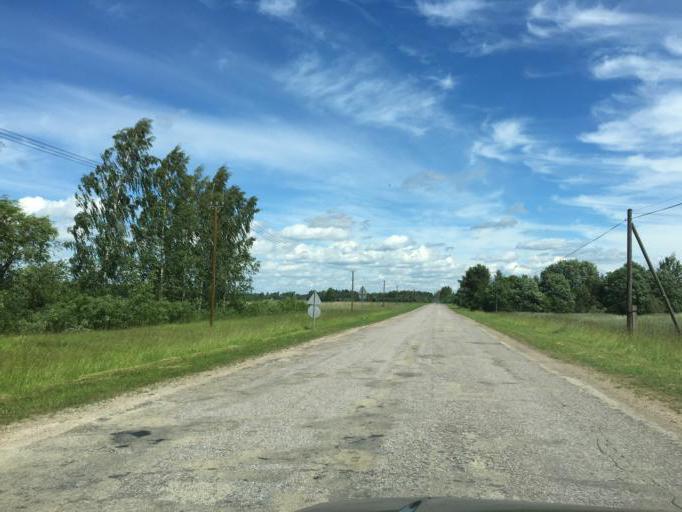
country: LV
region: Balvu Rajons
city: Balvi
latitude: 57.1513
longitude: 27.3096
